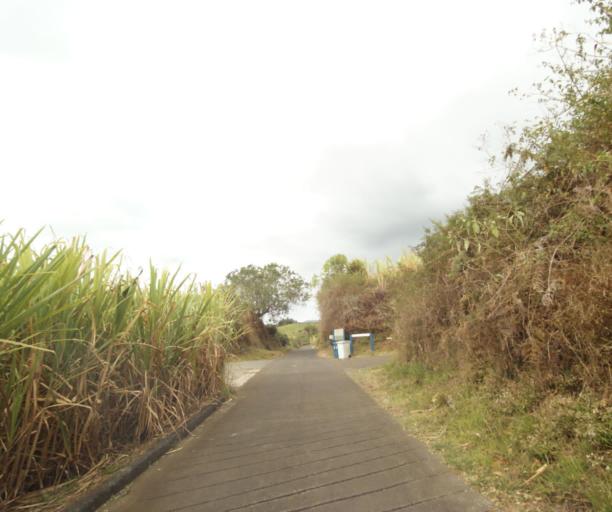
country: RE
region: Reunion
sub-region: Reunion
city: Saint-Paul
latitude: -21.0293
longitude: 55.3169
